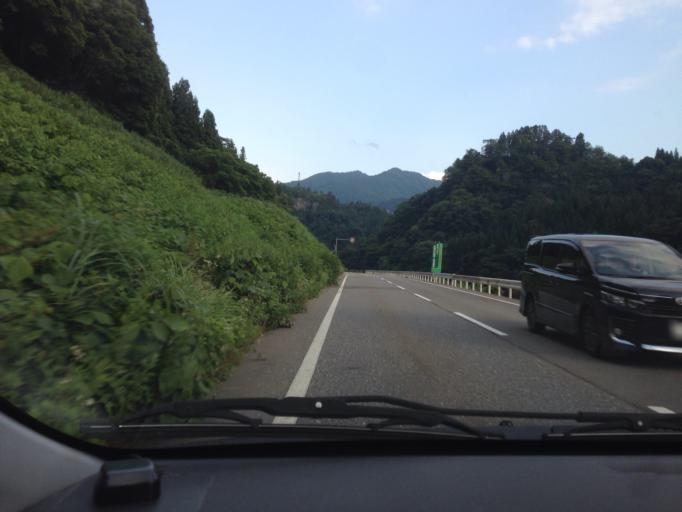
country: JP
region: Fukushima
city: Kitakata
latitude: 37.4759
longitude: 139.5882
